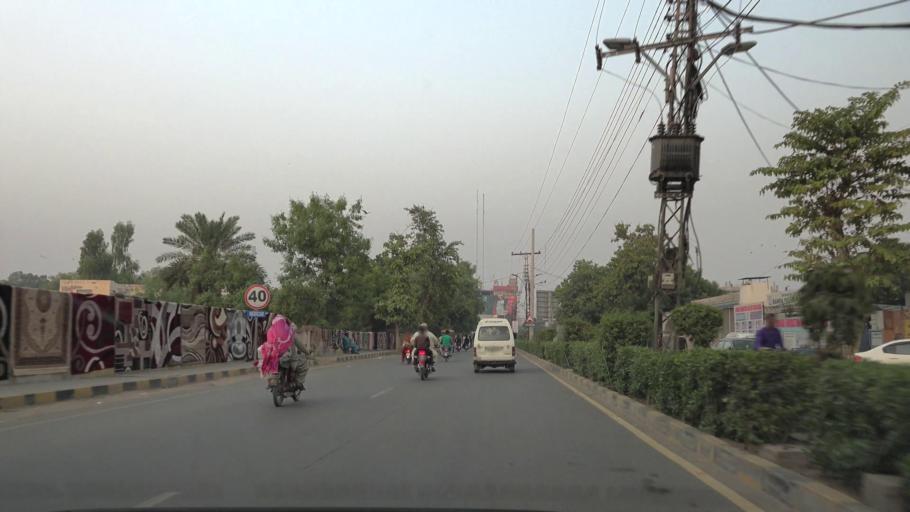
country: PK
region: Punjab
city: Faisalabad
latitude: 31.4093
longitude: 73.1099
